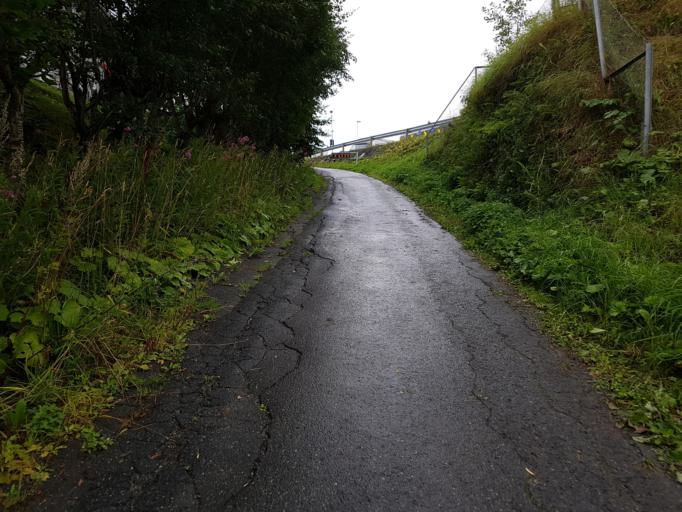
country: NO
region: Sor-Trondelag
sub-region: Trondheim
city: Trondheim
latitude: 63.3863
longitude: 10.4273
